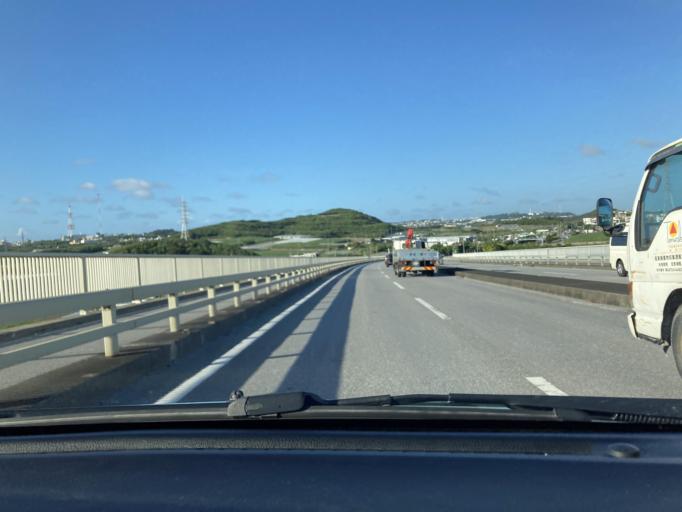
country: JP
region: Okinawa
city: Tomigusuku
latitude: 26.1674
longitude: 127.7078
